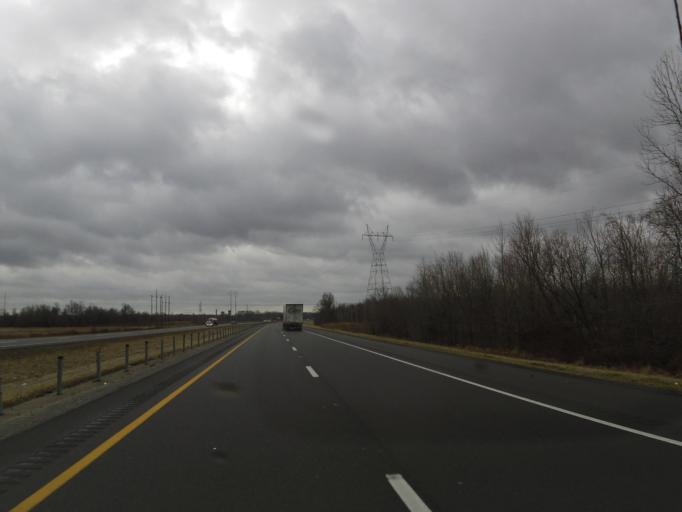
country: US
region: Kentucky
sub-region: McCracken County
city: Hendron
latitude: 37.0344
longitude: -88.6250
